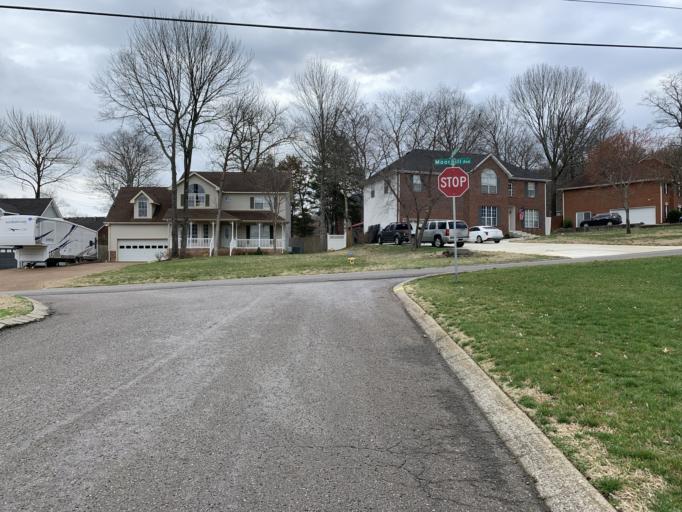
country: US
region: Tennessee
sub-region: Rutherford County
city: Smyrna
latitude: 35.9695
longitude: -86.5607
